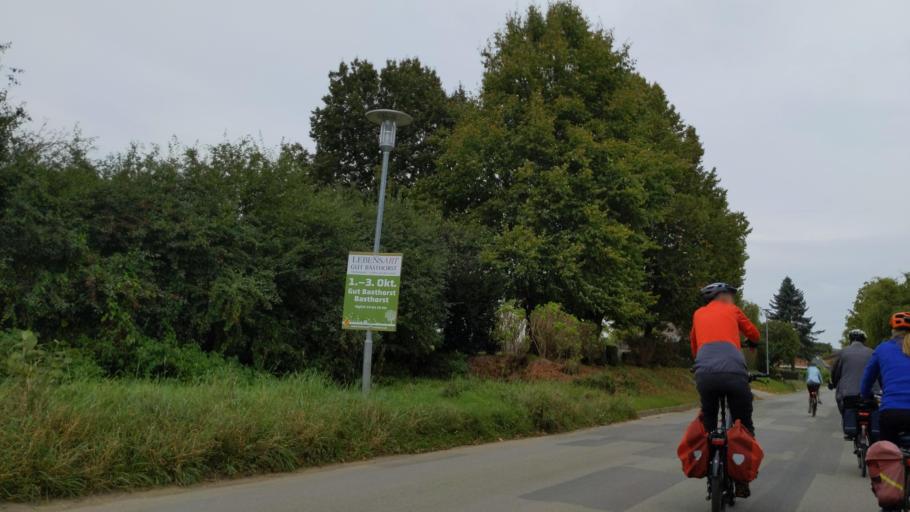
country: DE
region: Mecklenburg-Vorpommern
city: Schlagsdorf
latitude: 53.7346
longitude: 10.8258
